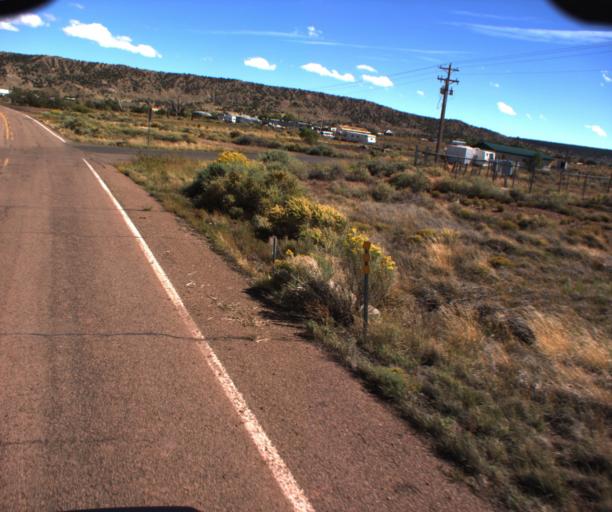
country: US
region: Arizona
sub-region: Apache County
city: Saint Johns
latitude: 34.4784
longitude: -109.6128
